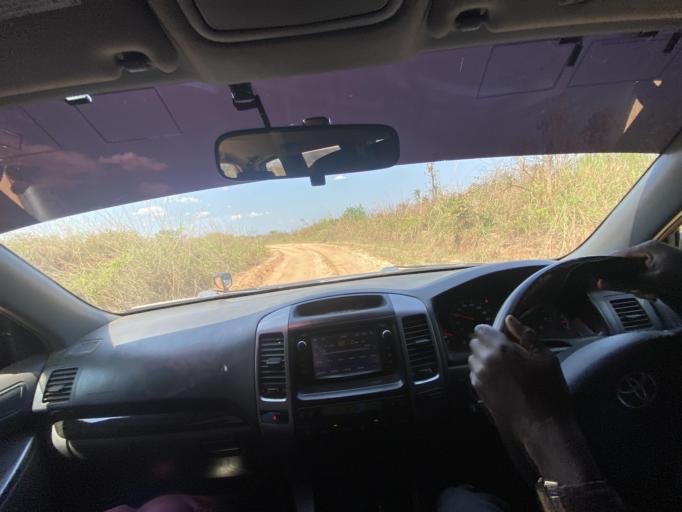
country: CD
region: Kasai-Oriental
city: Kabinda
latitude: -6.1323
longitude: 24.2472
